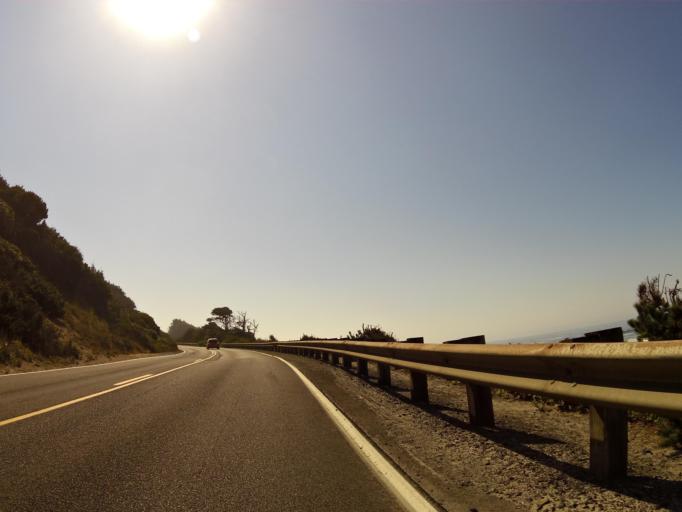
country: US
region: Oregon
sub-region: Tillamook County
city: Pacific City
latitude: 45.2402
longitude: -123.9693
